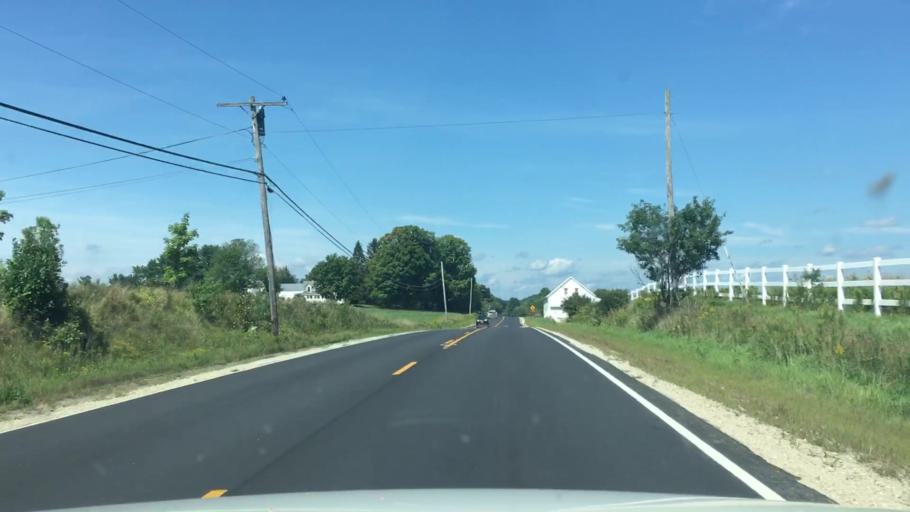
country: US
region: Maine
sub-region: Cumberland County
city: Cumberland Center
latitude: 43.7850
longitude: -70.3043
